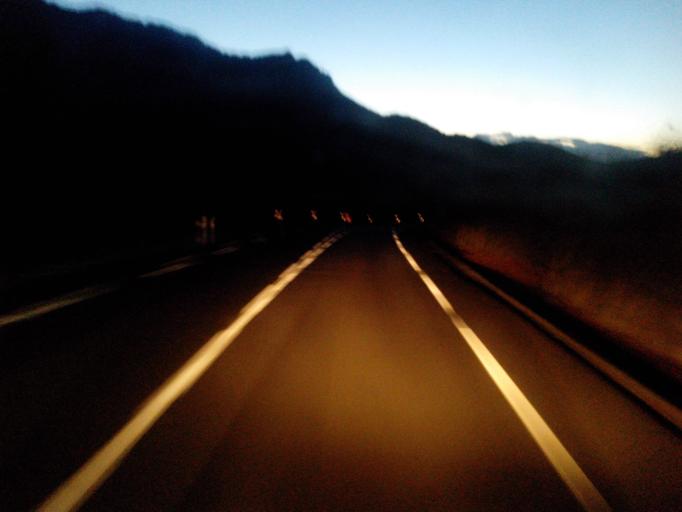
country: FR
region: Languedoc-Roussillon
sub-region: Departement des Pyrenees-Orientales
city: Saint-Paul-de-Fenouillet
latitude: 42.8144
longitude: 2.5486
